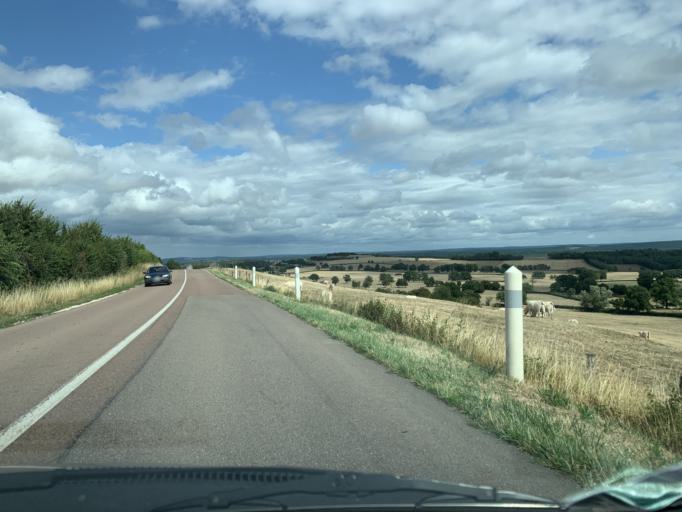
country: FR
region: Bourgogne
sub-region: Departement de la Nievre
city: Varzy
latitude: 47.3778
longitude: 3.4325
